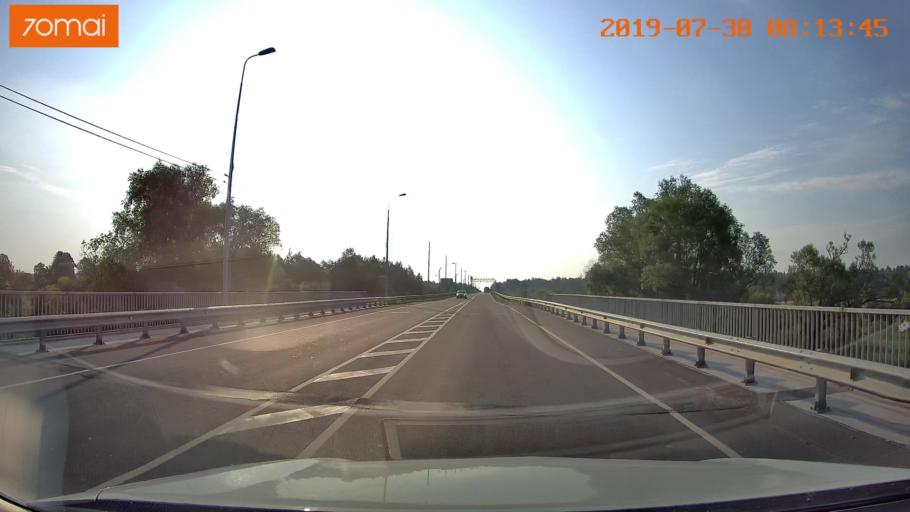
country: RU
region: Kaliningrad
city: Gvardeysk
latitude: 54.6488
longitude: 21.3561
